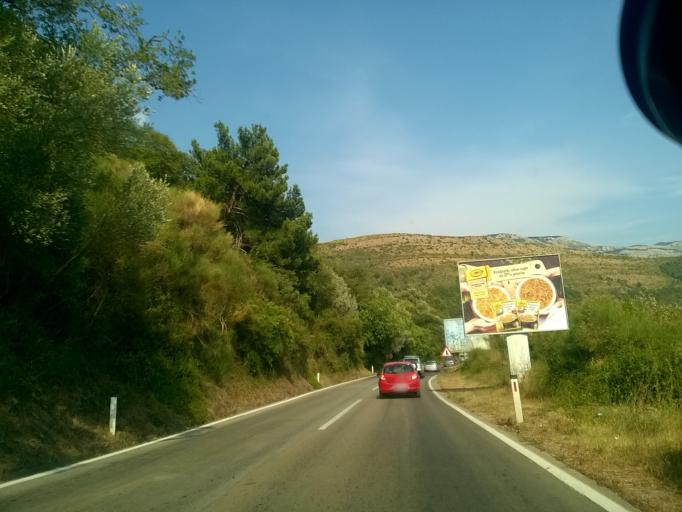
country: ME
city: Petrovac na Moru
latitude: 42.2101
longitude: 18.9356
